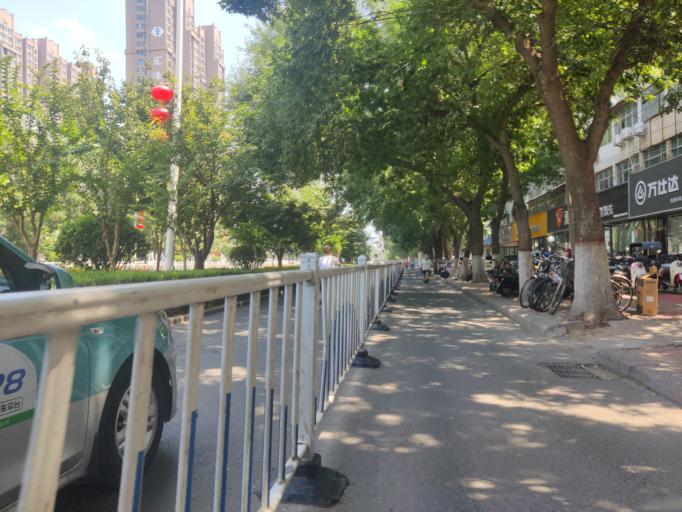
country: CN
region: Henan Sheng
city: Puyang
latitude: 35.7720
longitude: 115.0313
